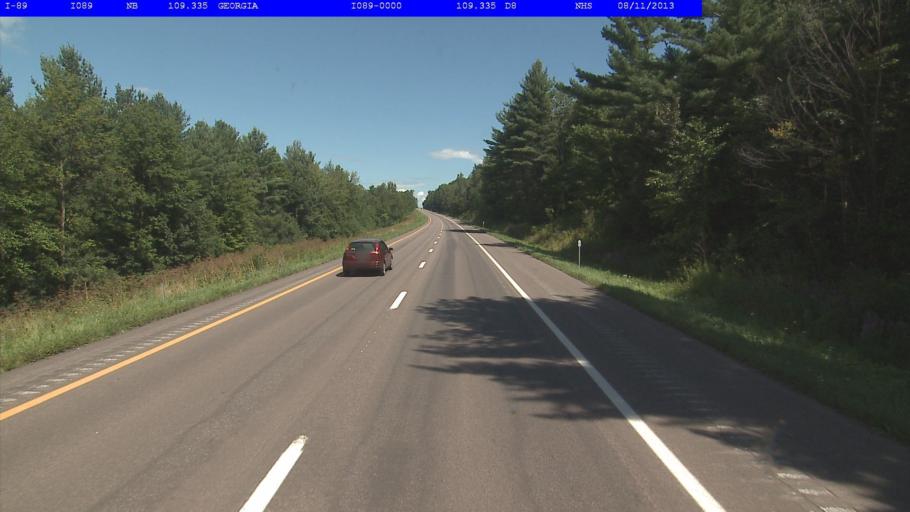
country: US
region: Vermont
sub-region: Franklin County
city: Saint Albans
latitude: 44.7314
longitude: -73.0798
